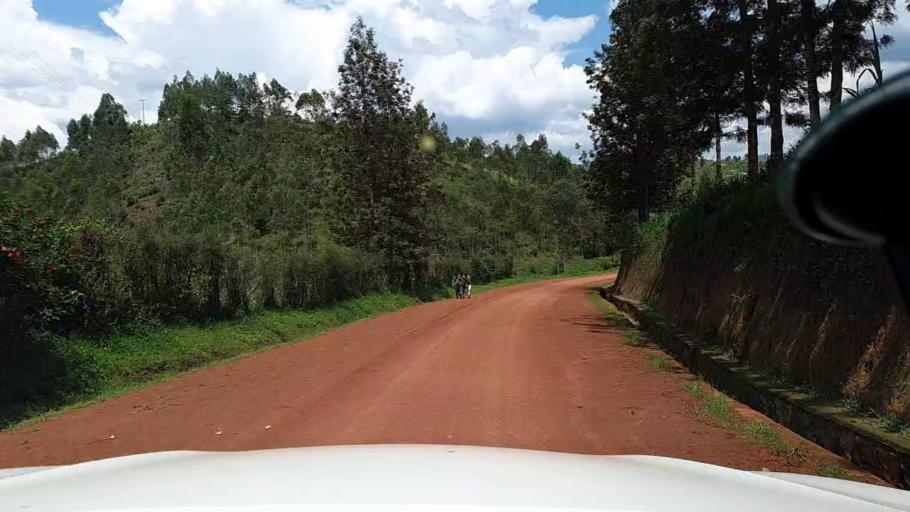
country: RW
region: Northern Province
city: Byumba
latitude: -1.7027
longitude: 29.8366
